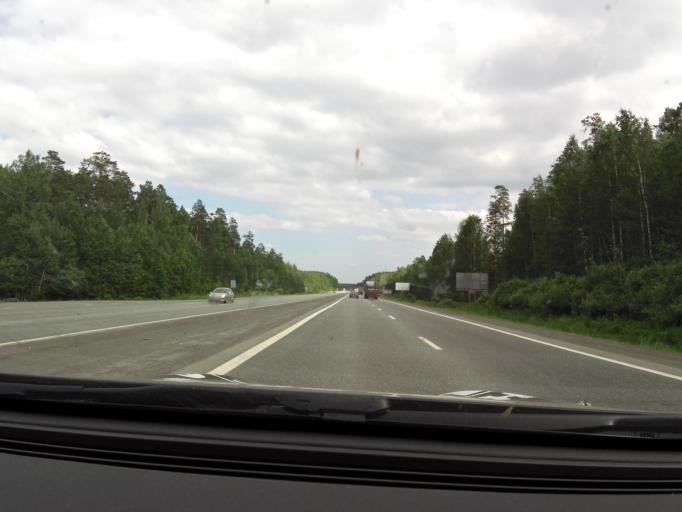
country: RU
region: Sverdlovsk
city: Talitsa
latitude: 56.8454
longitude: 60.0861
